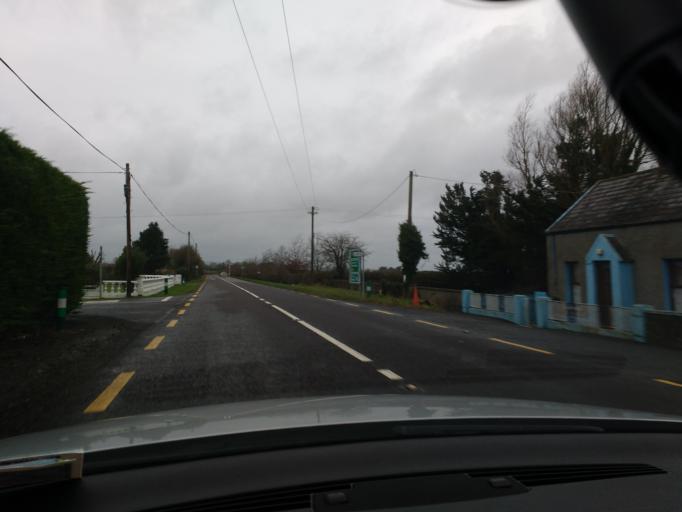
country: IE
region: Munster
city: Thurles
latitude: 52.6720
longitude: -7.7421
